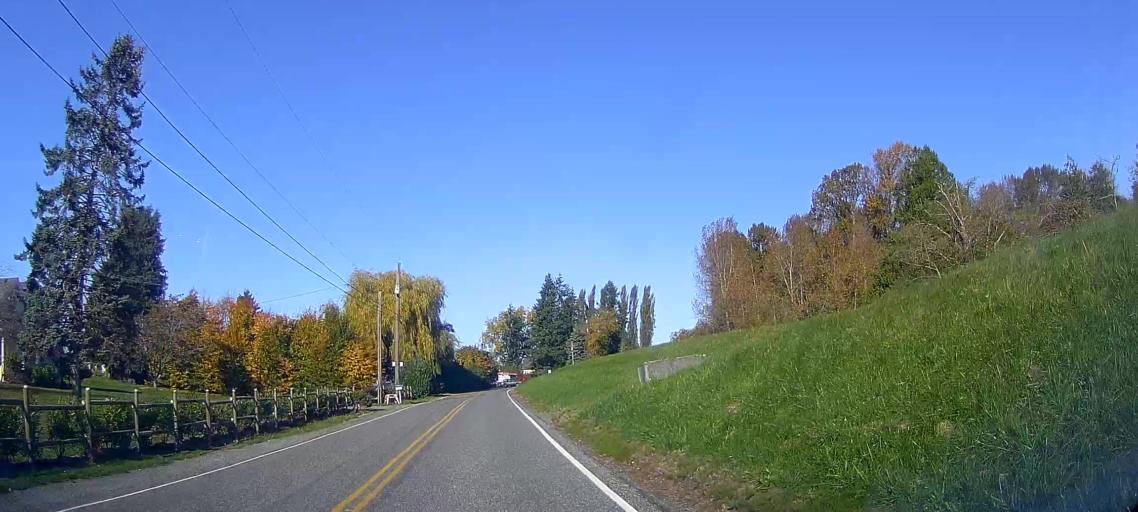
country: US
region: Washington
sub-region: Skagit County
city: Mount Vernon
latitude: 48.4091
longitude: -122.3683
